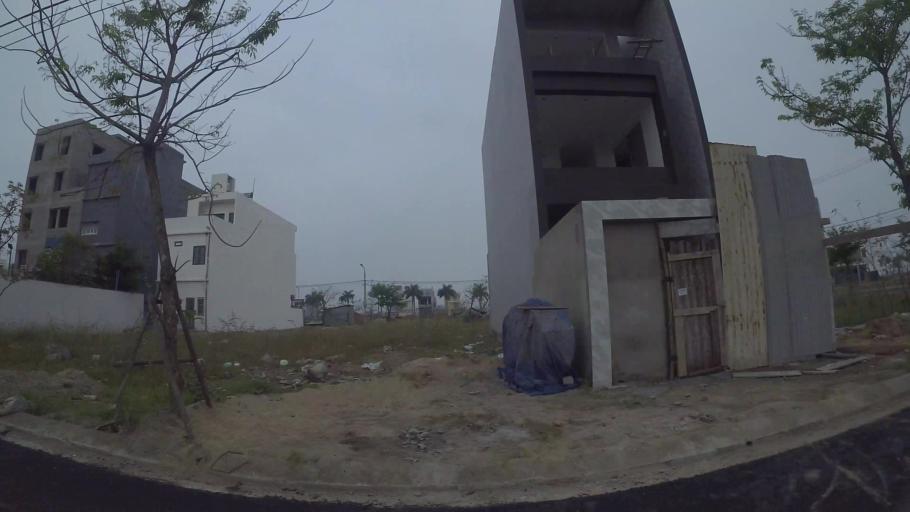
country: VN
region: Da Nang
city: Ngu Hanh Son
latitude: 16.0218
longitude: 108.2339
